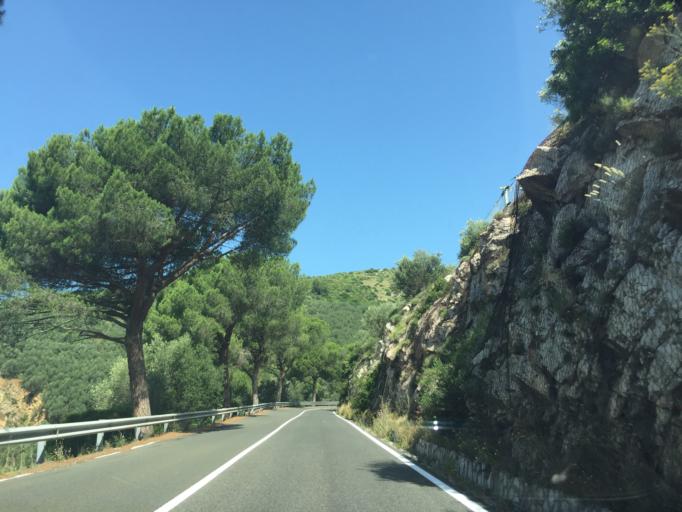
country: IT
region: Tuscany
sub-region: Province of Pisa
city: San Giuliano Terme
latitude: 43.7651
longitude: 10.4473
